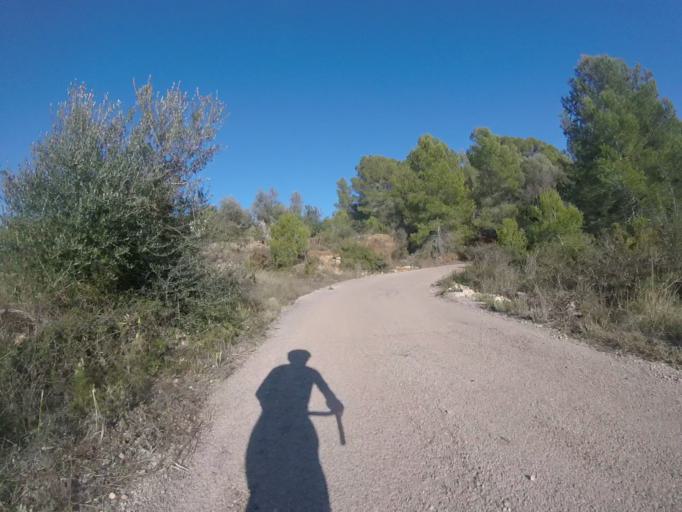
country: ES
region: Valencia
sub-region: Provincia de Castello
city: Sarratella
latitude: 40.2882
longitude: 0.0734
